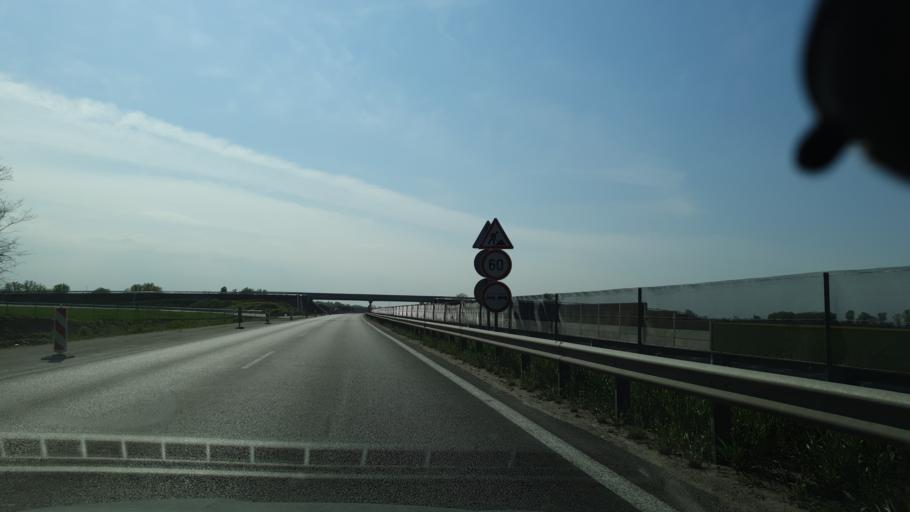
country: HU
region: Pest
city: Tortel
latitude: 47.1917
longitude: 19.9236
